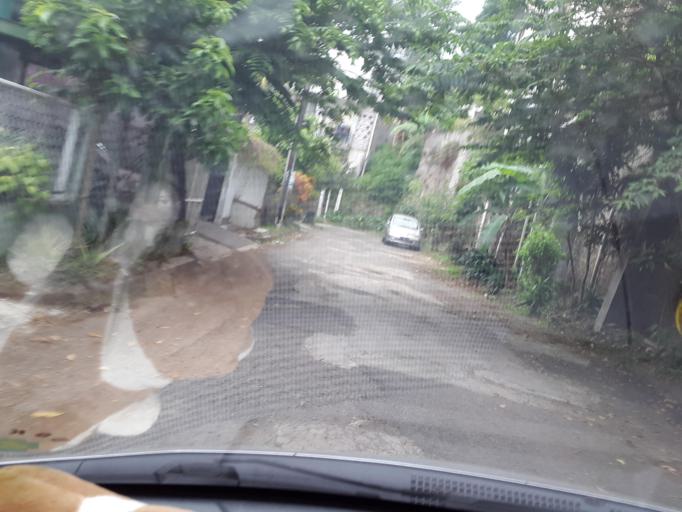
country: ID
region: West Java
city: Bandung
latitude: -6.8834
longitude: 107.6501
